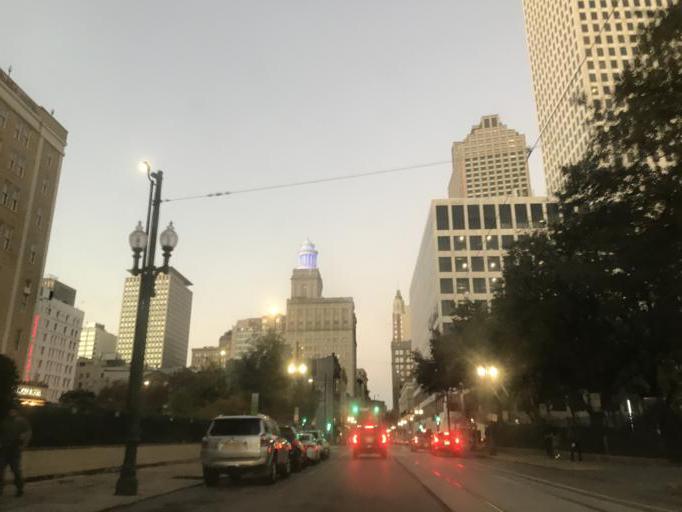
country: US
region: Louisiana
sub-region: Orleans Parish
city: New Orleans
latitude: 29.9491
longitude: -90.0721
